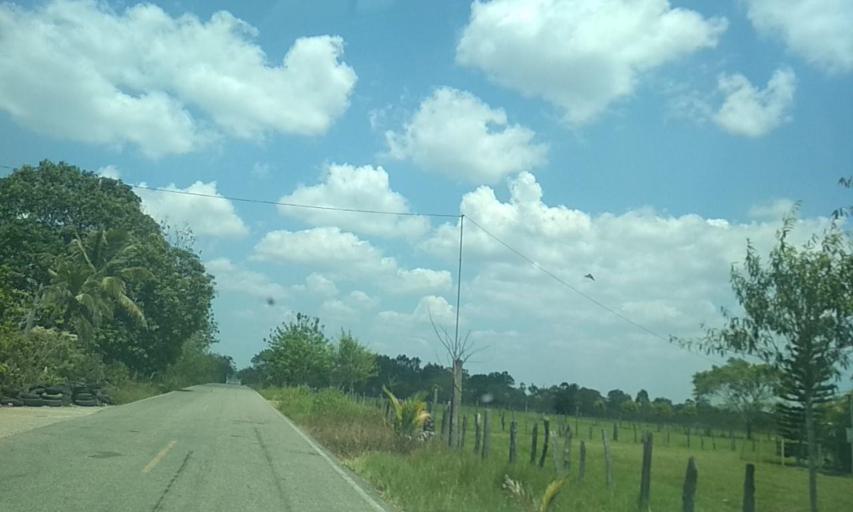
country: MX
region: Tabasco
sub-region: Huimanguillo
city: Huapacal 1ra. Seccion
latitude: 17.7538
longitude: -93.7454
